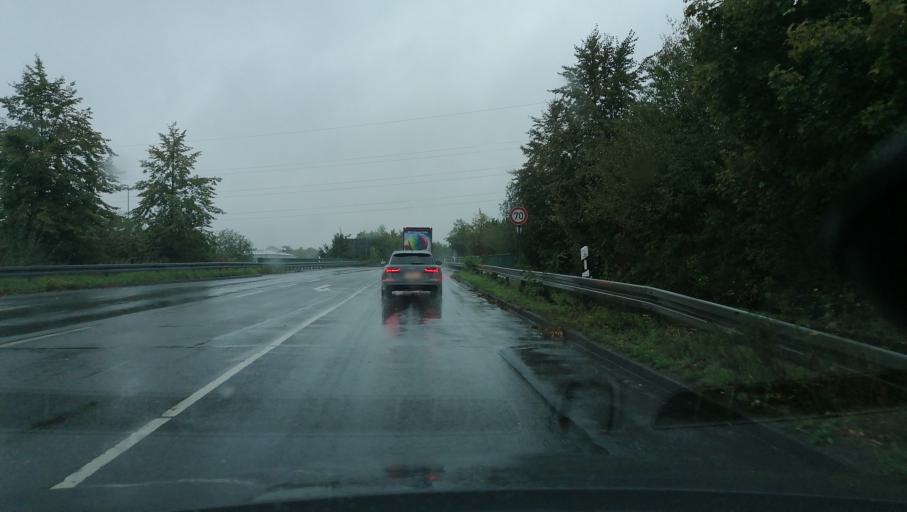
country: DE
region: North Rhine-Westphalia
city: Oer-Erkenschwick
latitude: 51.5984
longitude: 7.2481
